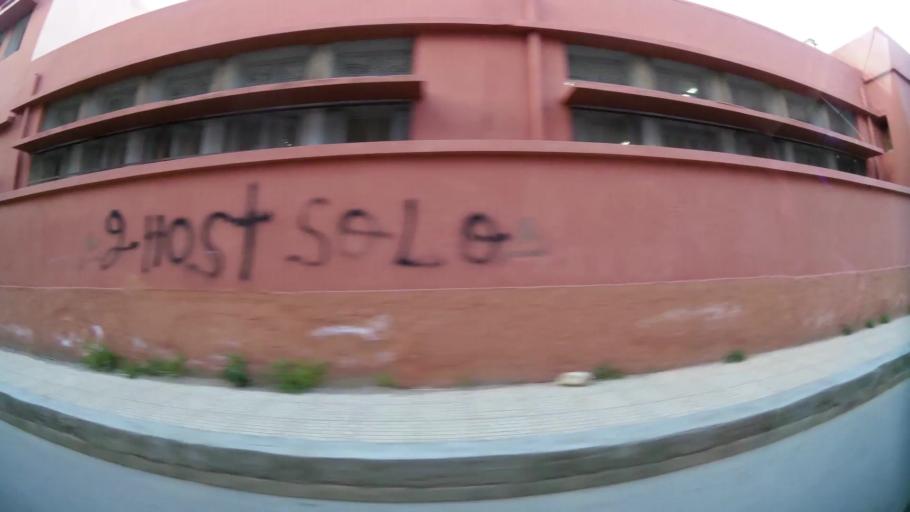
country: MA
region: Oriental
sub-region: Berkane-Taourirt
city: Berkane
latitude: 34.9268
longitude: -2.3290
